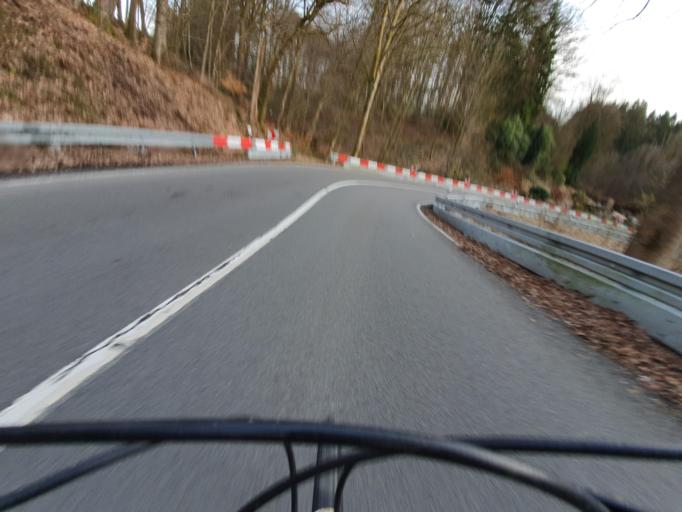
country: DE
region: North Rhine-Westphalia
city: Burscheid
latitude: 51.0886
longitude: 7.1742
